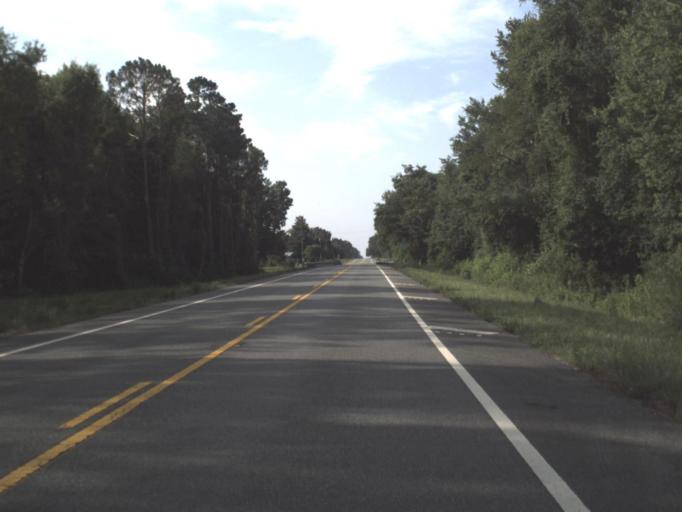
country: US
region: Florida
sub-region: Taylor County
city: Perry
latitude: 30.2551
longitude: -83.6238
